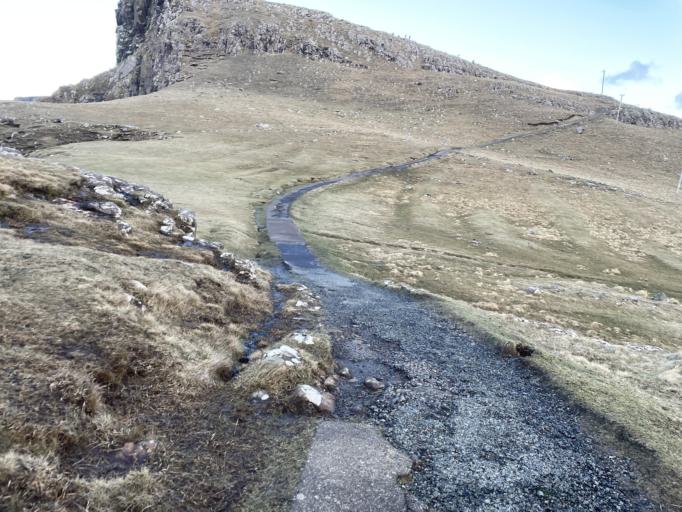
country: GB
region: Scotland
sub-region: Eilean Siar
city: Harris
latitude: 57.4247
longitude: -6.7855
